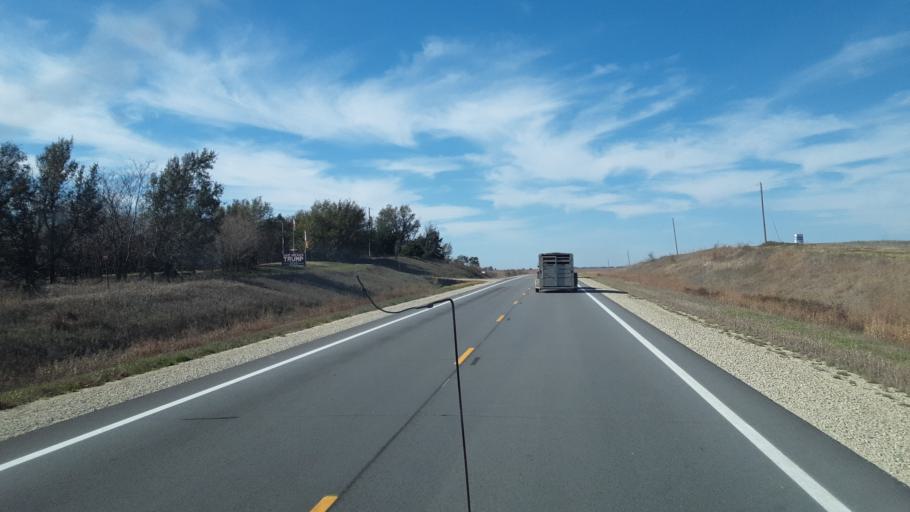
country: US
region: Kansas
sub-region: Marion County
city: Marion
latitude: 38.3625
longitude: -96.8607
